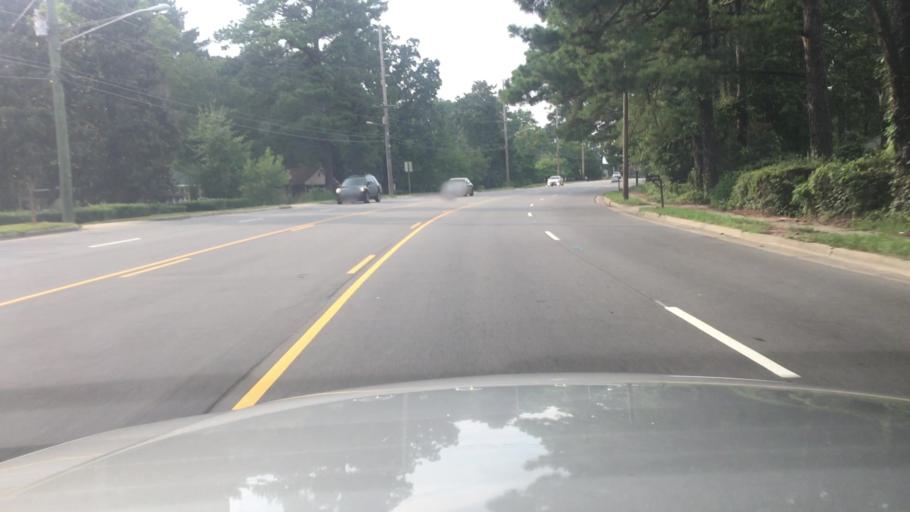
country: US
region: North Carolina
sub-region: Cumberland County
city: Fayetteville
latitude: 35.0614
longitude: -78.9495
